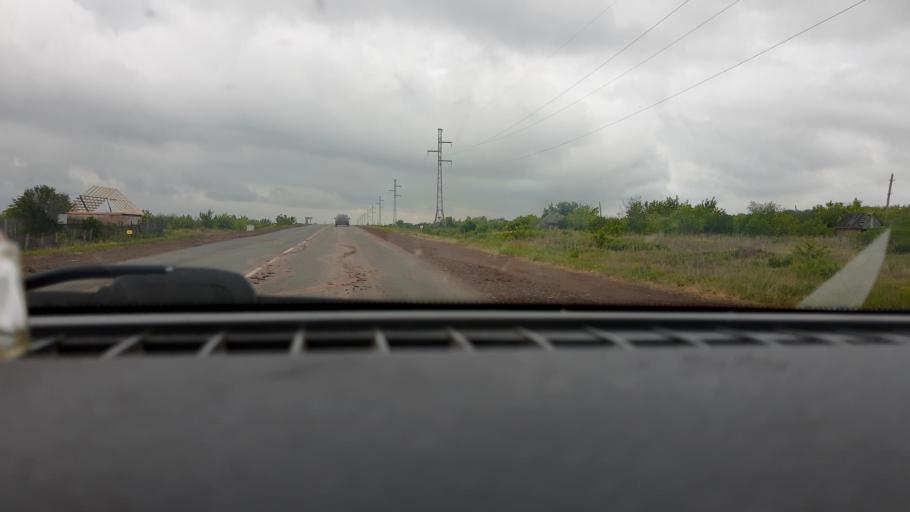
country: RU
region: Bashkortostan
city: Priyutovo
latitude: 53.9089
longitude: 53.9453
